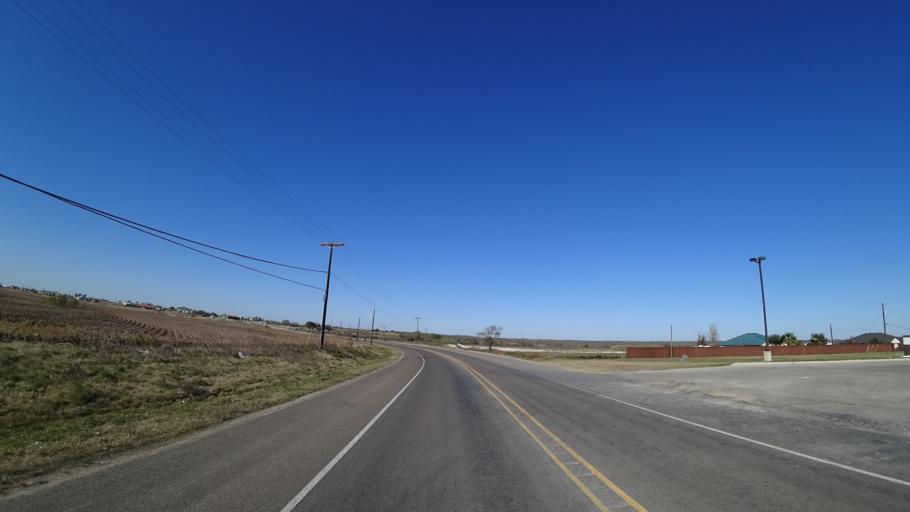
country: US
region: Texas
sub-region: Travis County
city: Garfield
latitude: 30.1015
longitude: -97.6077
